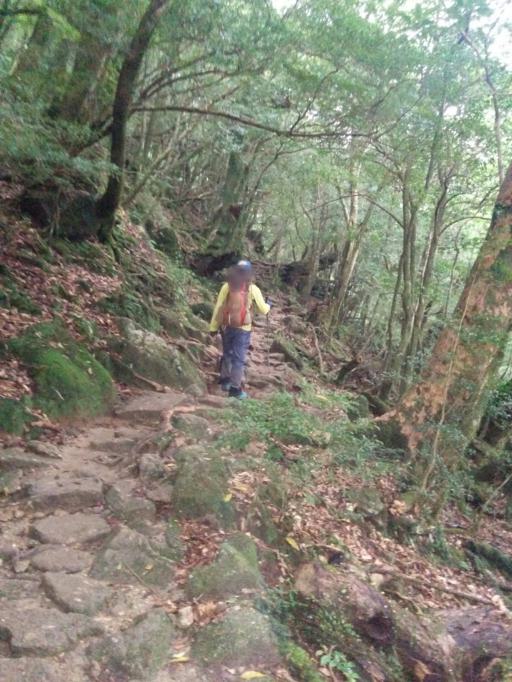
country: JP
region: Kagoshima
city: Nishinoomote
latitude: 30.3762
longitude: 130.5716
